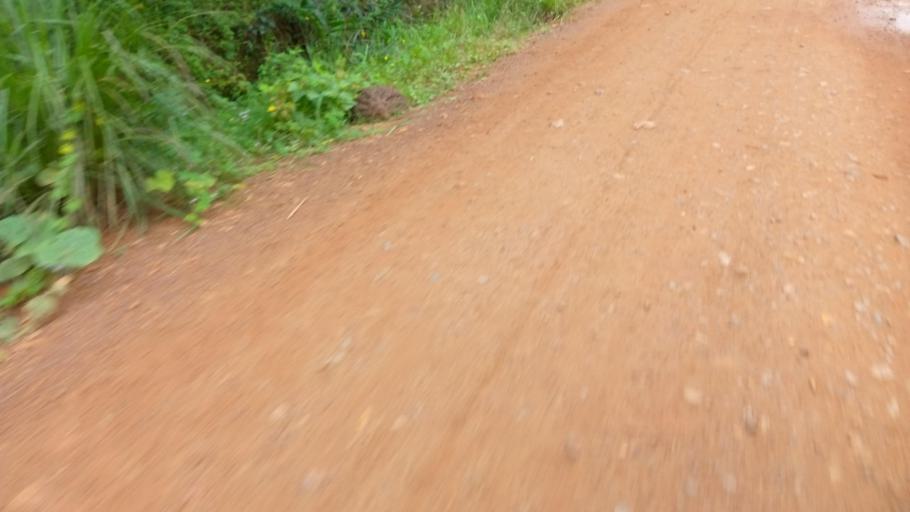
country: SL
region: Southern Province
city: Tongole
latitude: 7.4375
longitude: -11.8451
